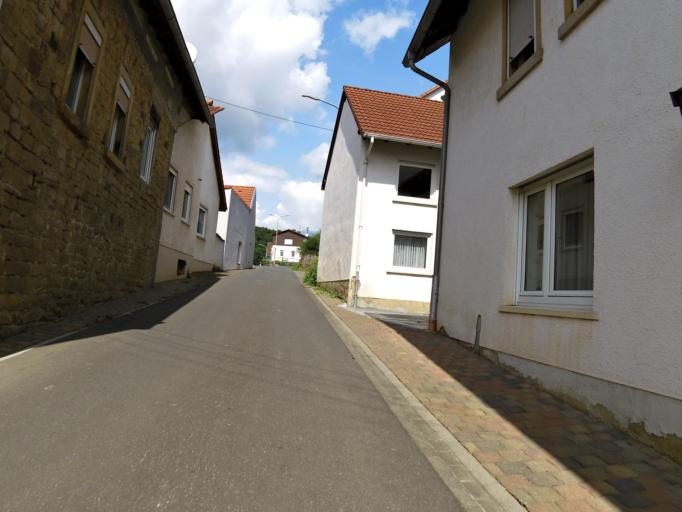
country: DE
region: Rheinland-Pfalz
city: Munsterappel
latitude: 49.7351
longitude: 7.8800
